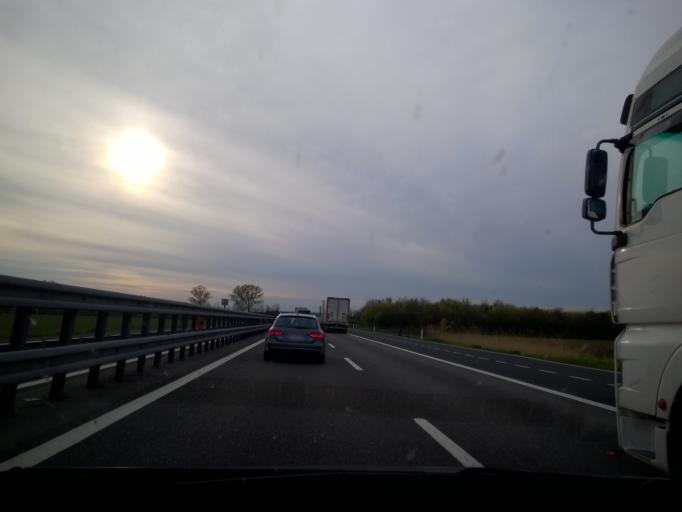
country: IT
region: Emilia-Romagna
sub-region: Provincia di Piacenza
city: Sarmato
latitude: 45.0673
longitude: 9.5199
